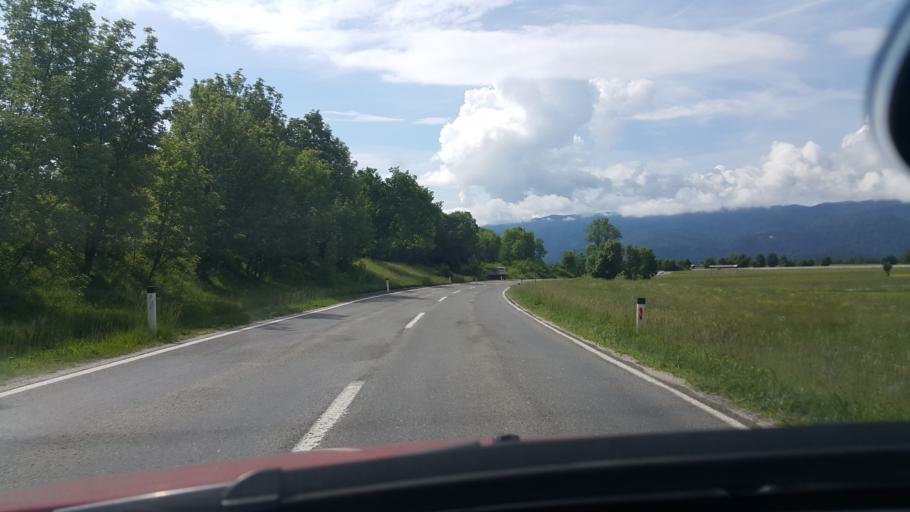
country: SI
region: Zirovnica
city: Zirovnica
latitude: 46.3960
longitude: 14.1373
